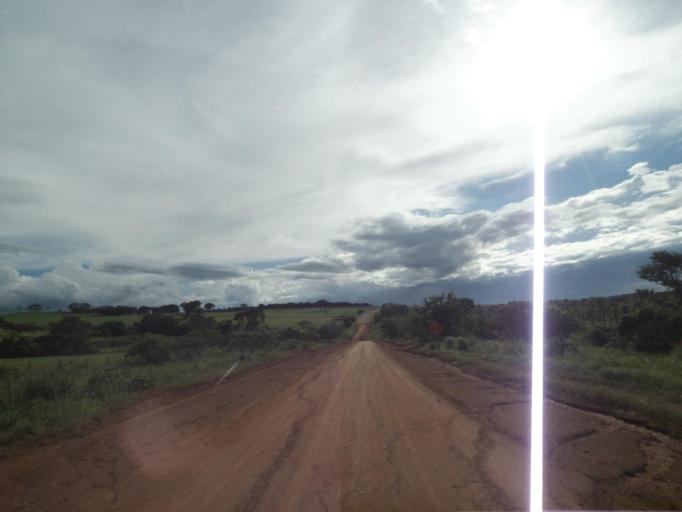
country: BR
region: Goias
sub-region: Jaragua
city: Jaragua
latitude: -15.8968
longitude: -49.5235
